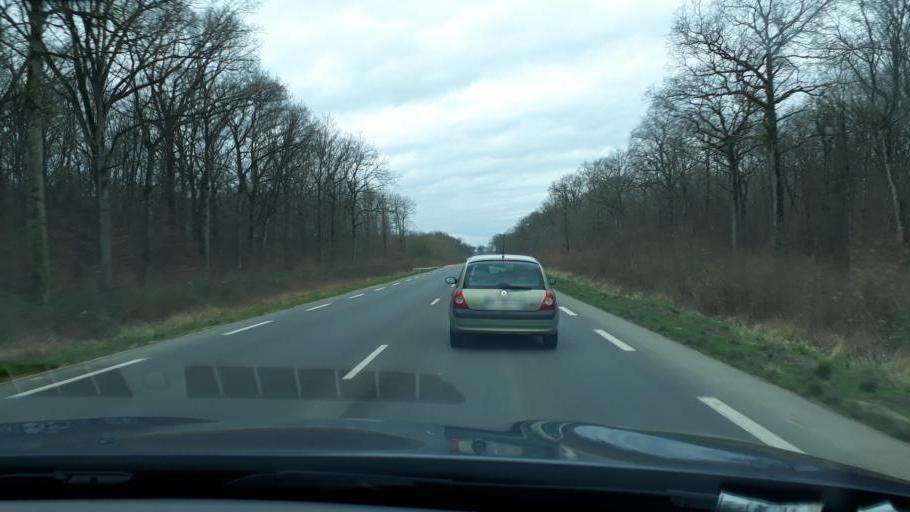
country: FR
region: Centre
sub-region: Departement du Loiret
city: Chanteau
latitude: 48.0048
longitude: 1.9510
